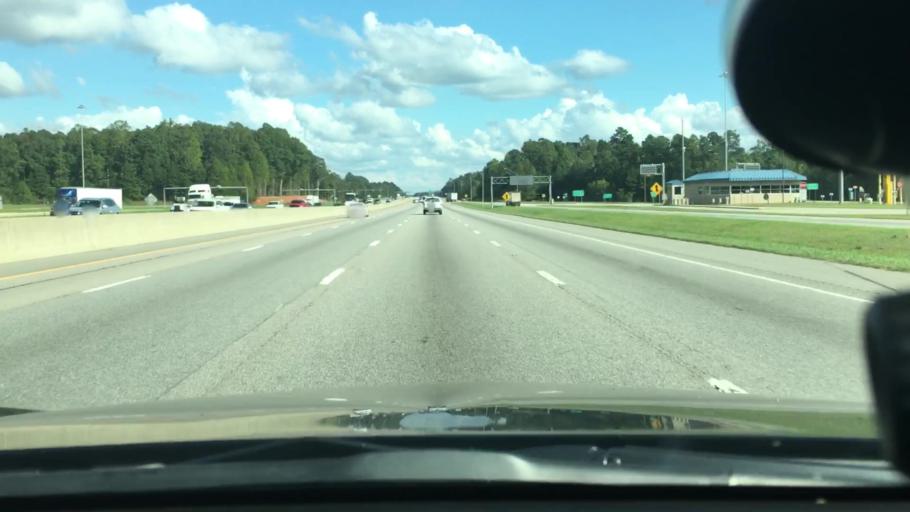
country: US
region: North Carolina
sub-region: Alamance County
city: Mebane
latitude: 36.0774
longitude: -79.2086
